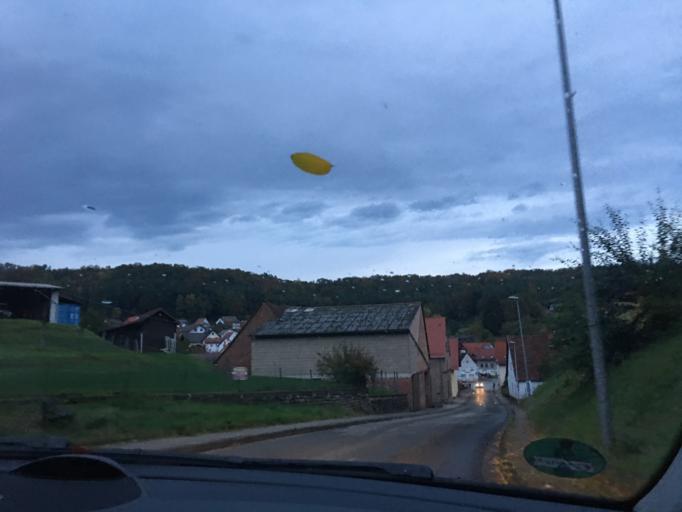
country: DE
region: Rheinland-Pfalz
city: Krickenbach
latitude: 49.3615
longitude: 7.6647
